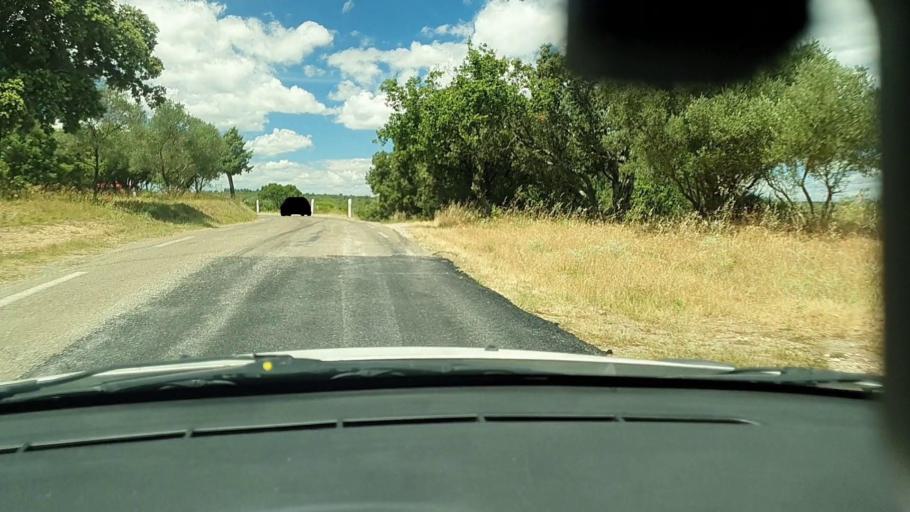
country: FR
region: Languedoc-Roussillon
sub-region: Departement du Gard
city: Poulx
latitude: 43.9558
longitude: 4.4467
